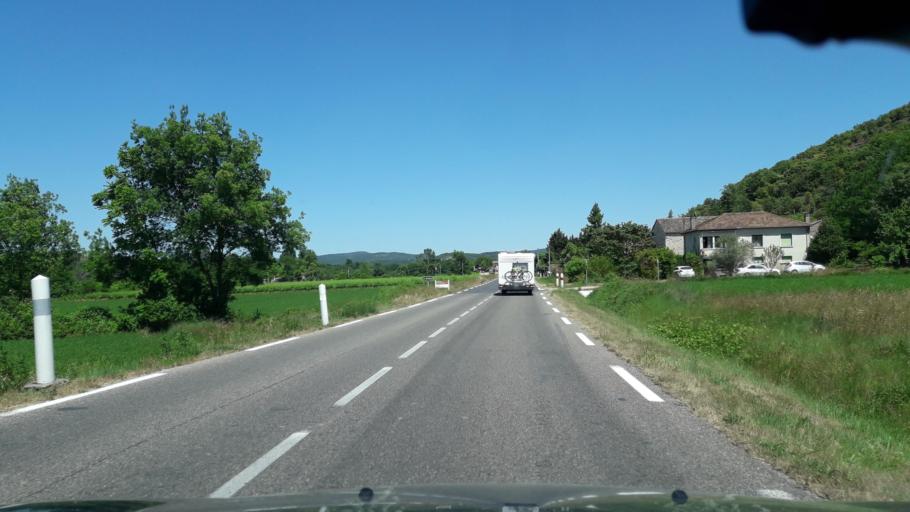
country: FR
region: Rhone-Alpes
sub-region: Departement de l'Ardeche
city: Ruoms
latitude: 44.4198
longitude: 4.3093
